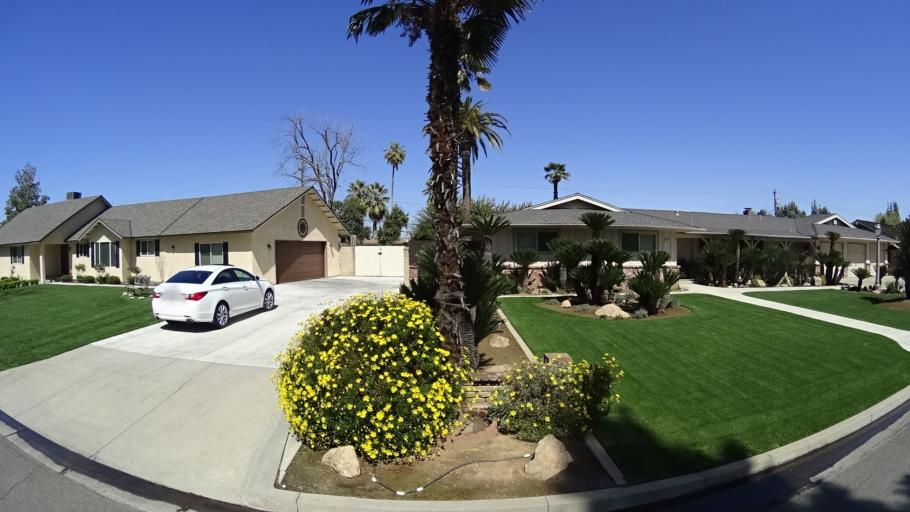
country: US
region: California
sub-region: Fresno County
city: Fresno
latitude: 36.8147
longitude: -119.8113
